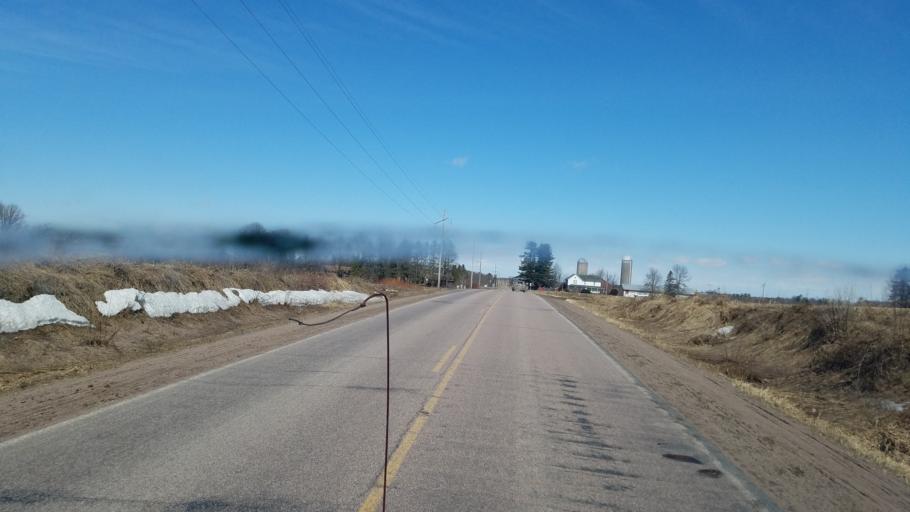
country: US
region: Wisconsin
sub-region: Clark County
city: Loyal
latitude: 44.5798
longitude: -90.3958
